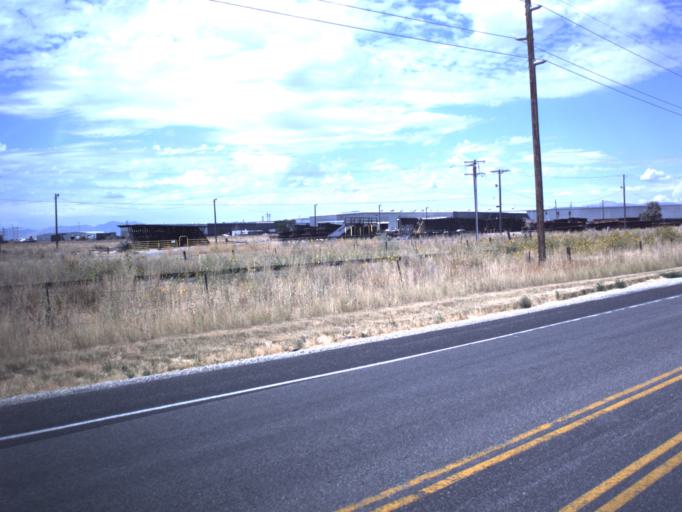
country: US
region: Utah
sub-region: Box Elder County
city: Brigham City
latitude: 41.5332
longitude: -112.0545
